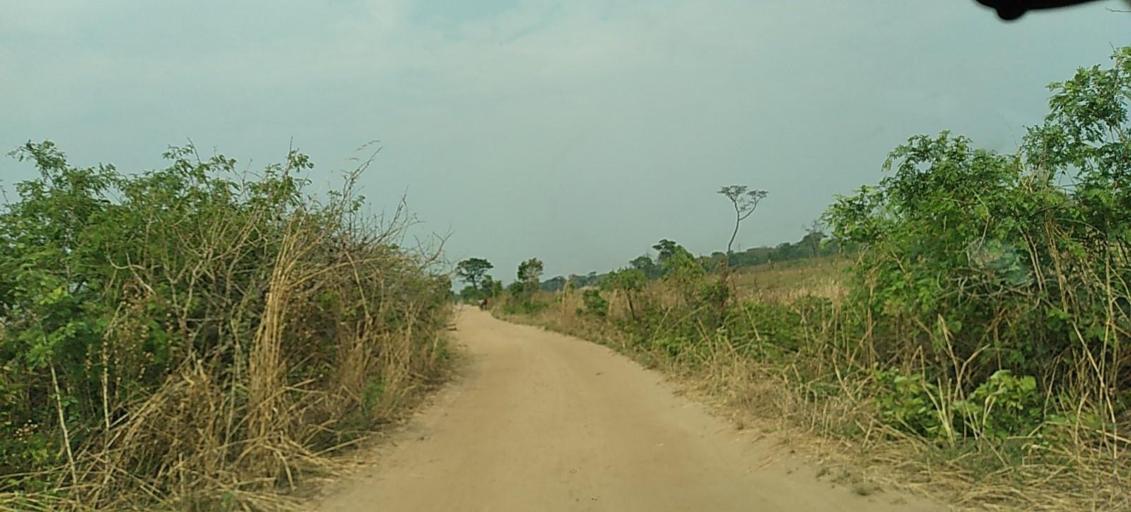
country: ZM
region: North-Western
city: Kabompo
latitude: -13.4802
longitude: 24.4192
